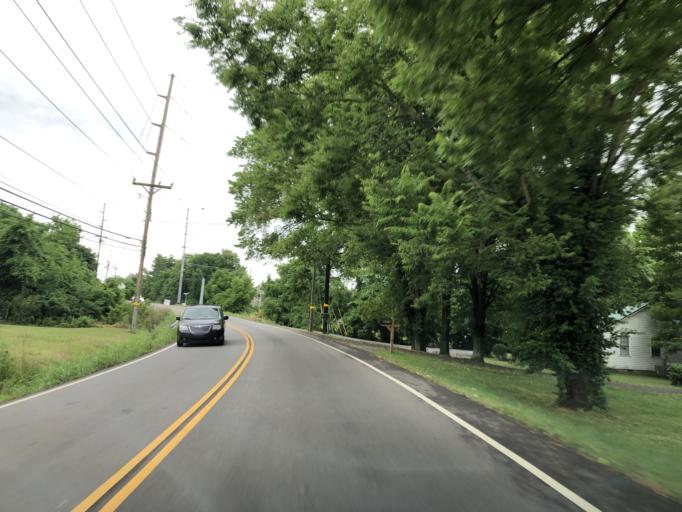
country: US
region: Tennessee
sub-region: Davidson County
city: Nashville
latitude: 36.2454
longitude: -86.7800
